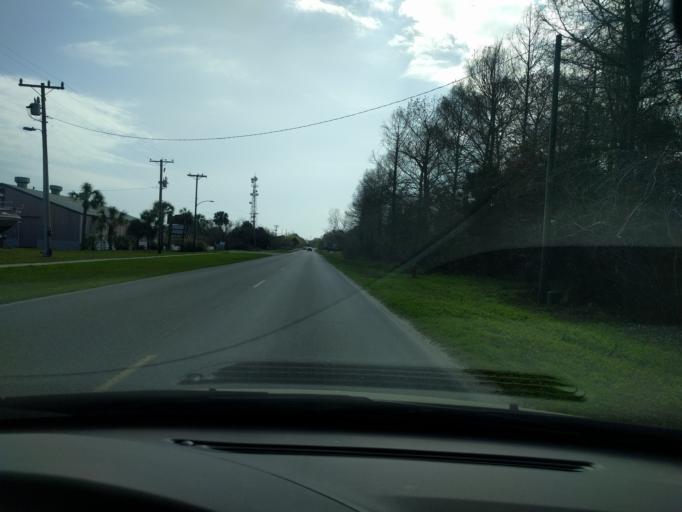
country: US
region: Florida
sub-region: Franklin County
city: Apalachicola
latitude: 29.7319
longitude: -84.9911
